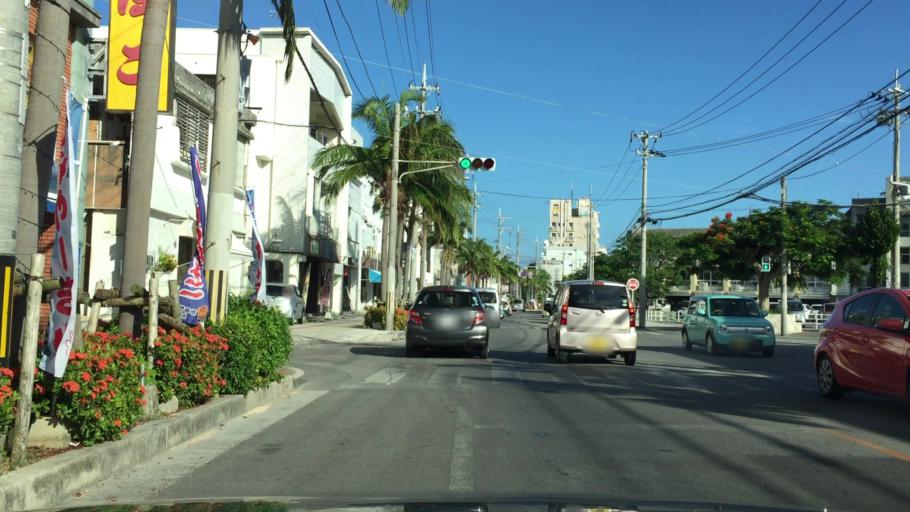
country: JP
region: Okinawa
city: Ishigaki
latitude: 24.3419
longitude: 124.1552
